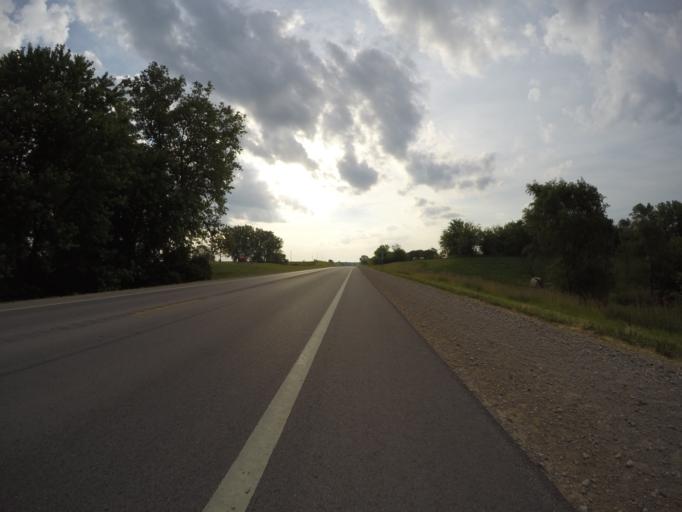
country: US
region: Kansas
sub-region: Doniphan County
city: Troy
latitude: 39.7928
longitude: -95.0662
